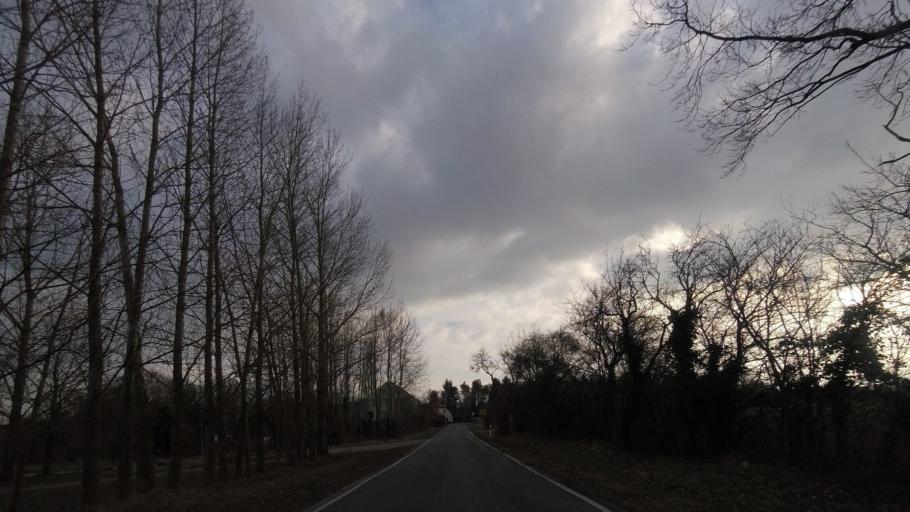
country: DE
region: Brandenburg
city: Wiesenburg
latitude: 52.1411
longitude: 12.5190
